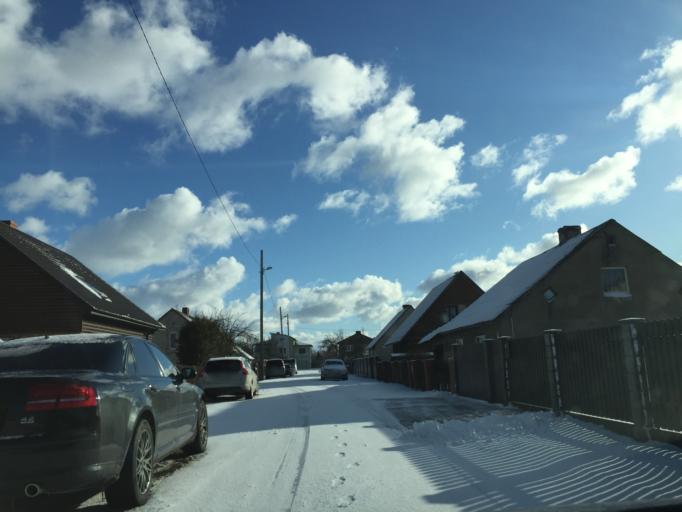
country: LV
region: Ventspils
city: Ventspils
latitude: 57.3798
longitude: 21.5650
